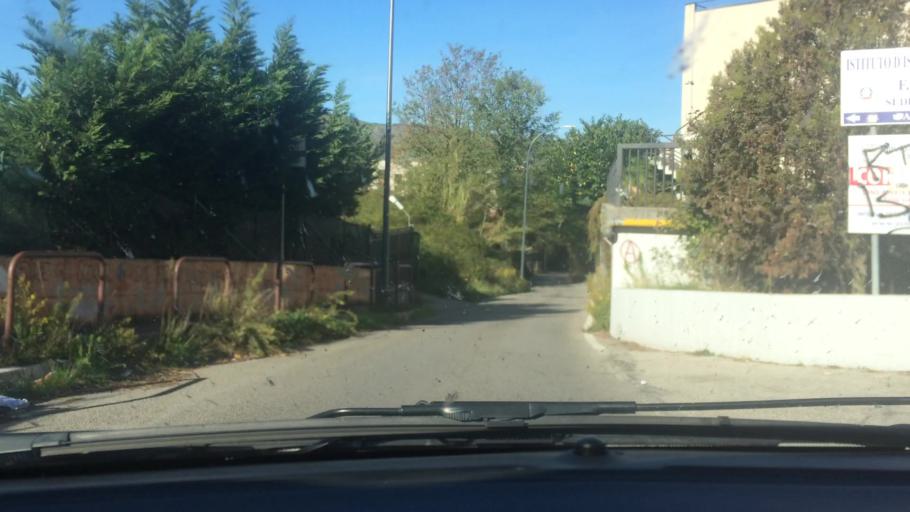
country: IT
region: Basilicate
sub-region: Provincia di Potenza
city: Potenza
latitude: 40.6419
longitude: 15.7933
